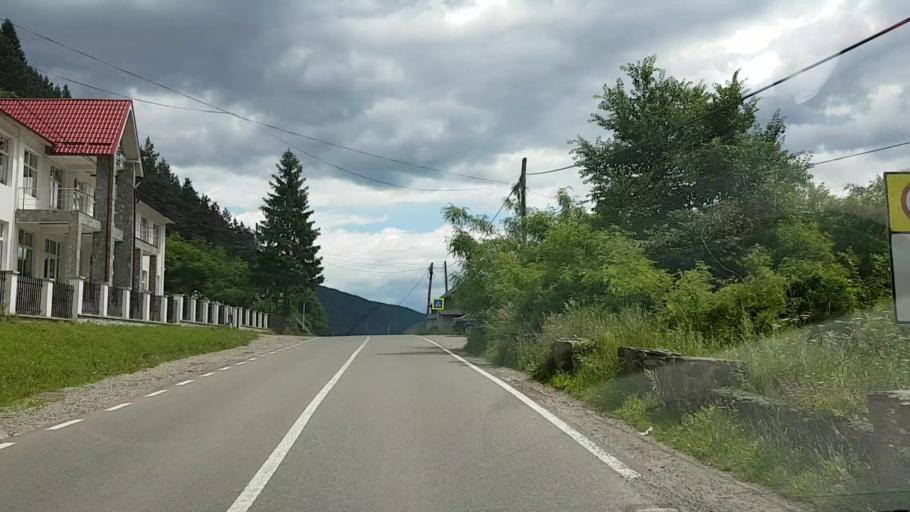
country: RO
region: Neamt
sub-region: Comuna Poiana Teiului
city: Poiana Teiului
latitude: 47.1204
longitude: 25.9120
